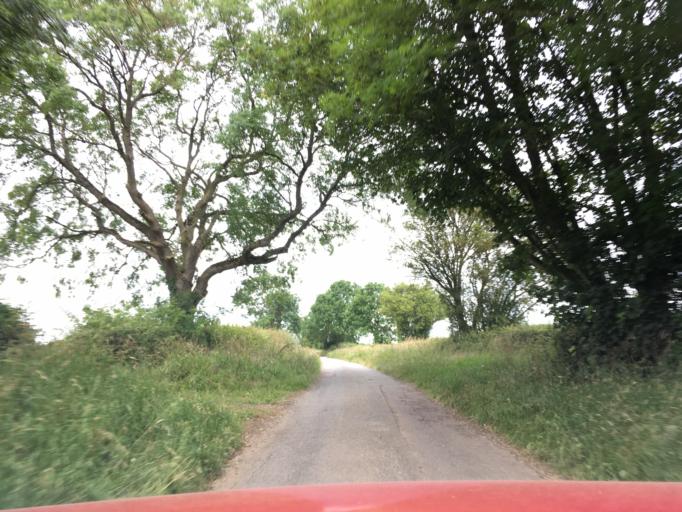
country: GB
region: England
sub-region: Oxfordshire
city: Charlbury
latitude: 51.9057
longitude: -1.5039
